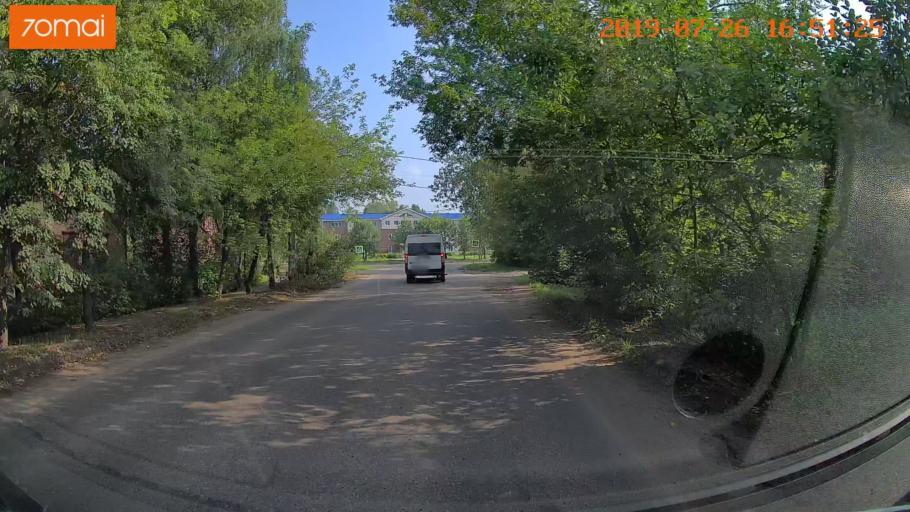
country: RU
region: Ivanovo
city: Bogorodskoye
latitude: 57.0188
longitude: 41.0215
